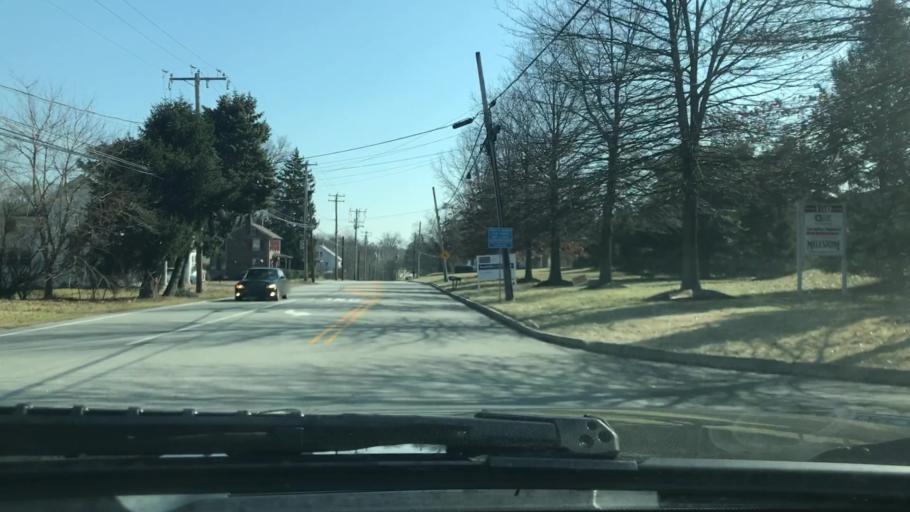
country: US
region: Pennsylvania
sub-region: Montgomery County
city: Audubon
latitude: 40.1357
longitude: -75.4665
